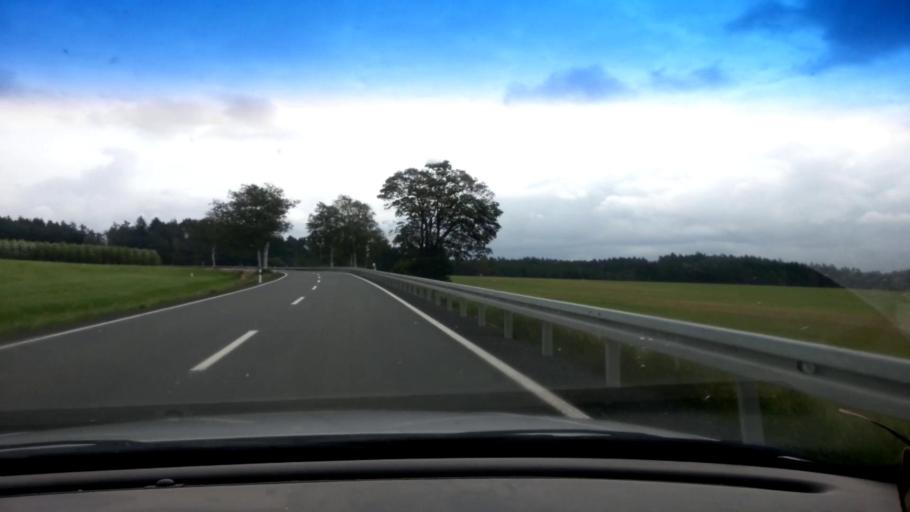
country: DE
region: Bavaria
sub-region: Upper Franconia
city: Roslau
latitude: 50.0767
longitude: 12.0185
